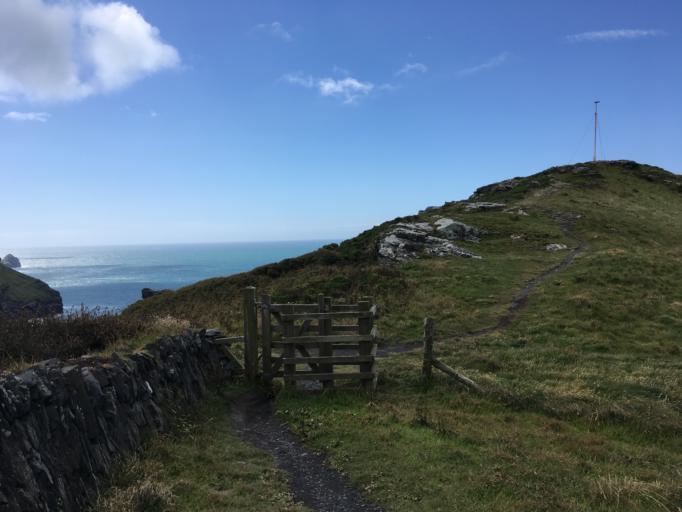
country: GB
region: England
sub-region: Cornwall
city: Tintagel
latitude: 50.6927
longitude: -4.6954
